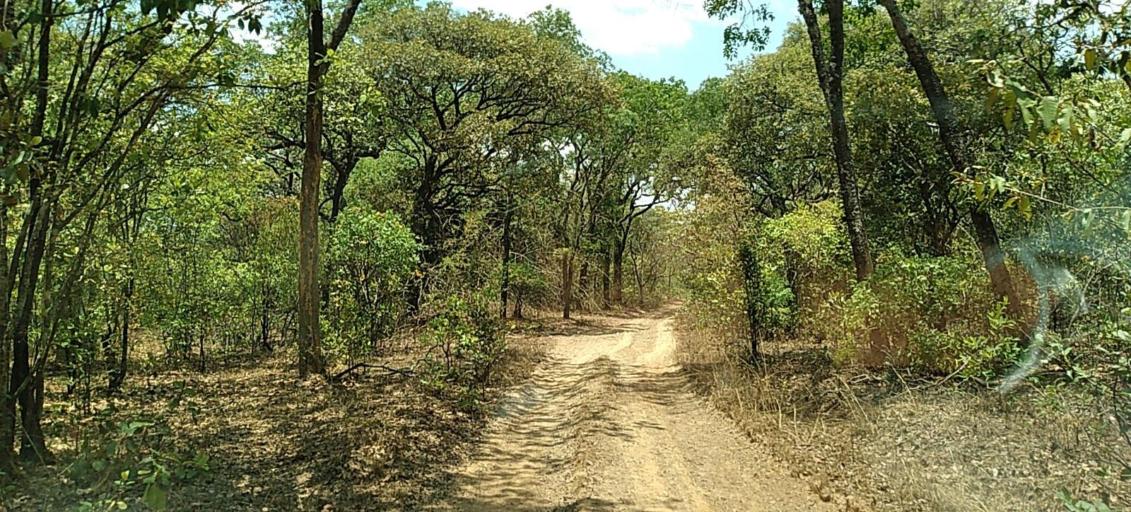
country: ZM
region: Copperbelt
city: Chililabombwe
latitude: -12.4678
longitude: 27.6997
